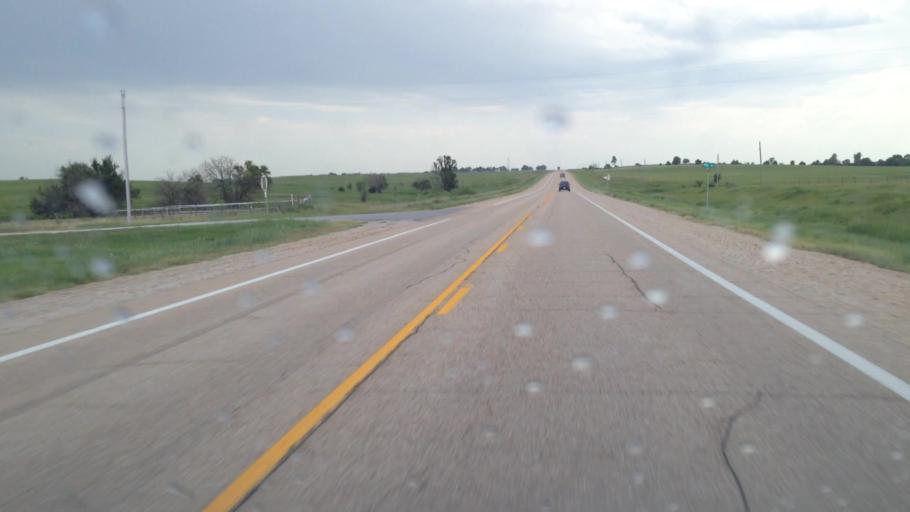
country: US
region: Kansas
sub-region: Coffey County
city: Burlington
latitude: 38.1562
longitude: -95.7391
